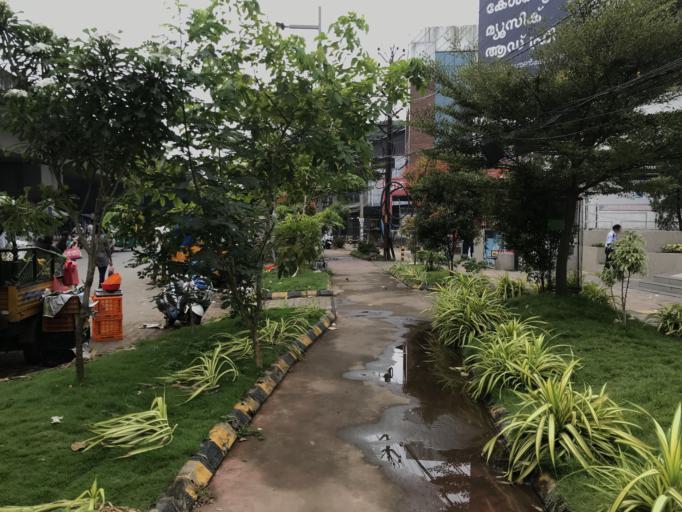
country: IN
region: Kerala
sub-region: Ernakulam
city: Aluva
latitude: 10.1078
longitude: 76.3495
